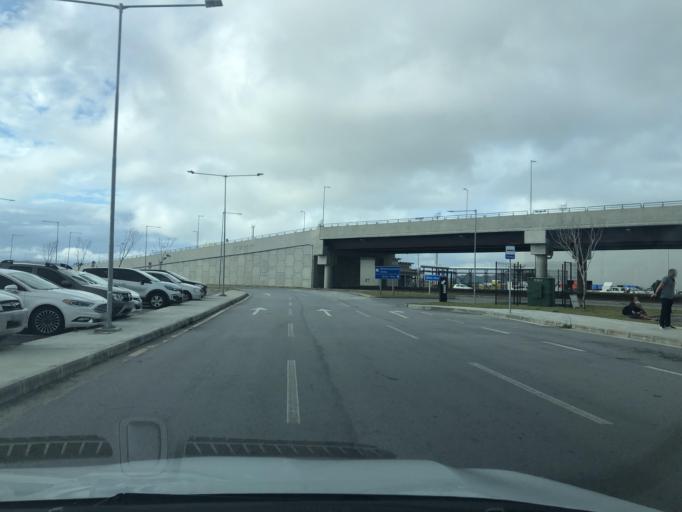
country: BR
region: Santa Catarina
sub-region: Florianopolis
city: Tapera
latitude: -27.6741
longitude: -48.5472
